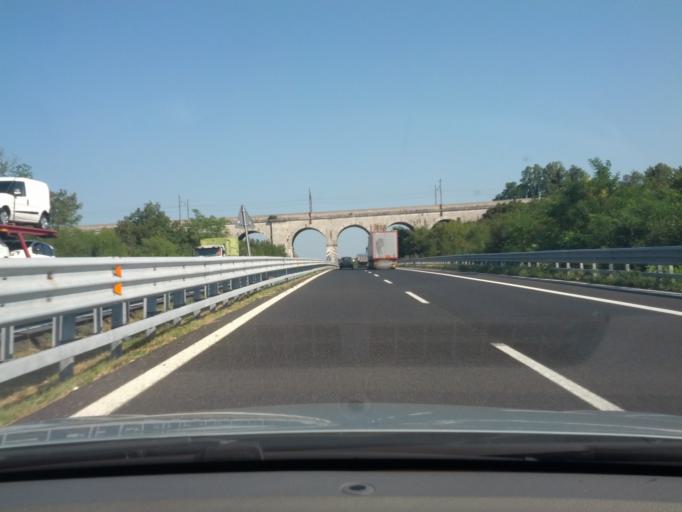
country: IT
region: Friuli Venezia Giulia
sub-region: Provincia di Trieste
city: Aurisina
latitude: 45.7542
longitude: 13.6750
